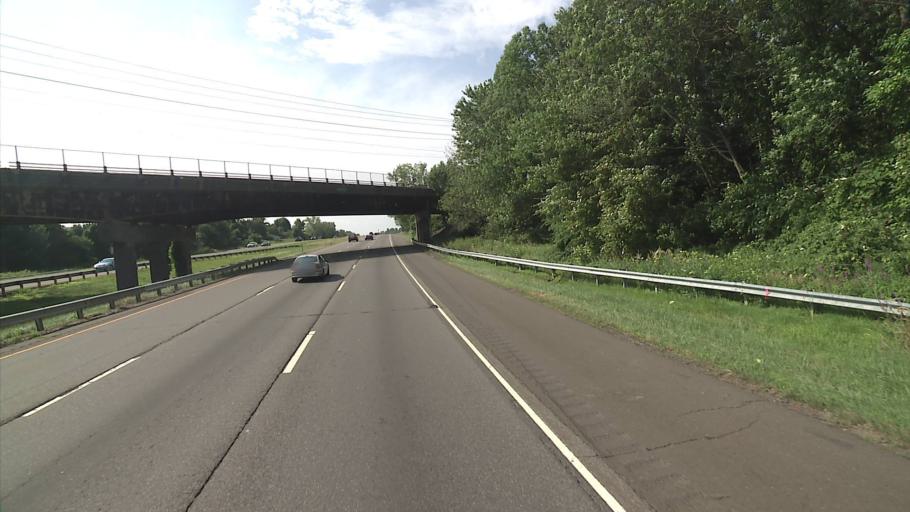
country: US
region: Connecticut
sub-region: New Haven County
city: Meriden
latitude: 41.5113
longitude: -72.7698
